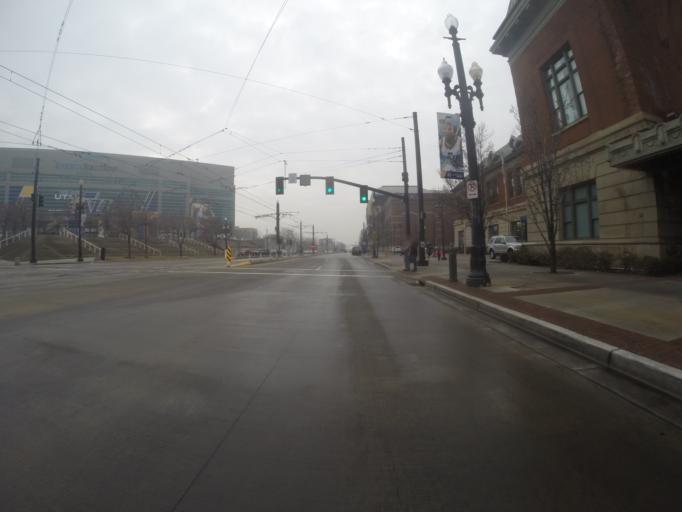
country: US
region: Utah
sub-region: Salt Lake County
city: Salt Lake City
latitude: 40.7693
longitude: -111.9027
